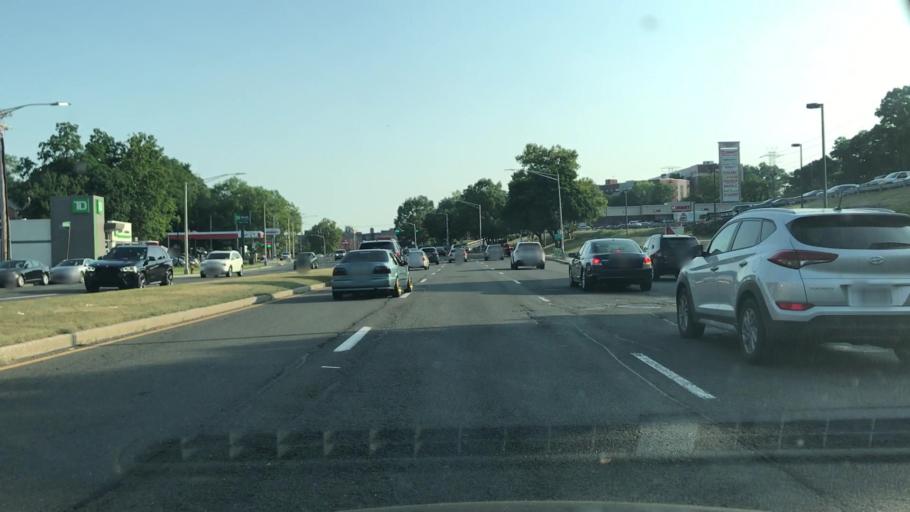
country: US
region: New York
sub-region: Westchester County
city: Tuckahoe
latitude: 40.9616
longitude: -73.8405
